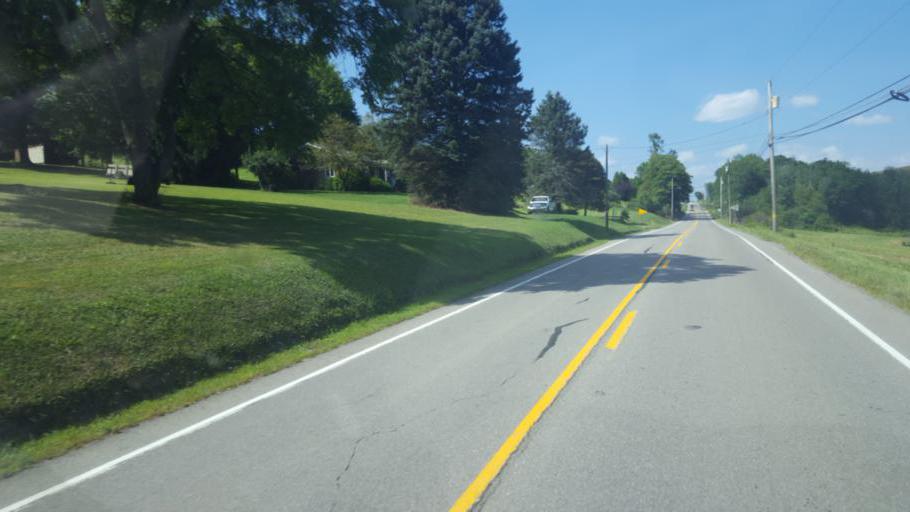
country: US
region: Pennsylvania
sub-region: Clarion County
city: Clarion
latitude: 41.1611
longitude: -79.3968
